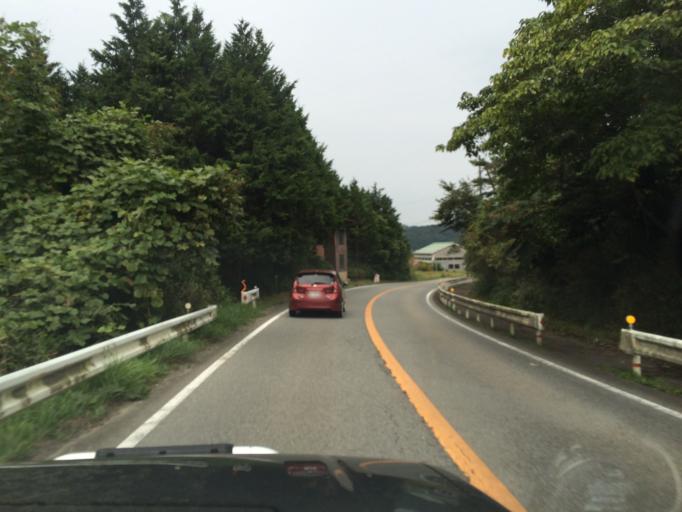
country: JP
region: Hyogo
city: Toyooka
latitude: 35.4125
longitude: 134.7834
